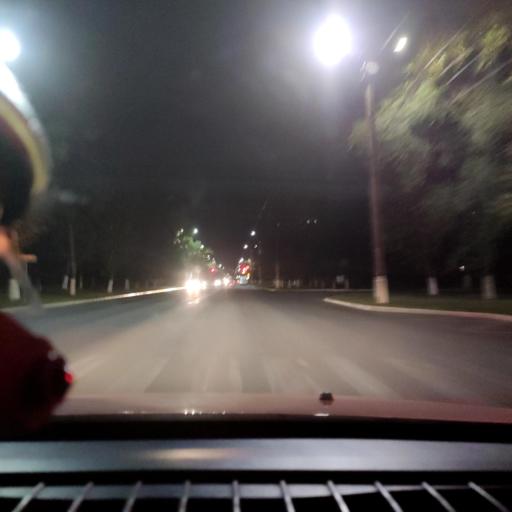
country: RU
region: Samara
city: Novokuybyshevsk
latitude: 53.0927
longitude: 49.9651
